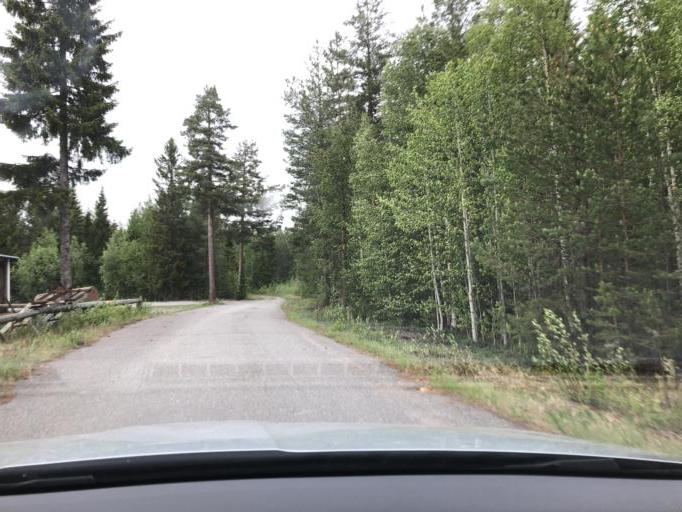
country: SE
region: Norrbotten
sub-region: Pitea Kommun
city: Roknas
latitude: 65.3923
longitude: 21.2693
